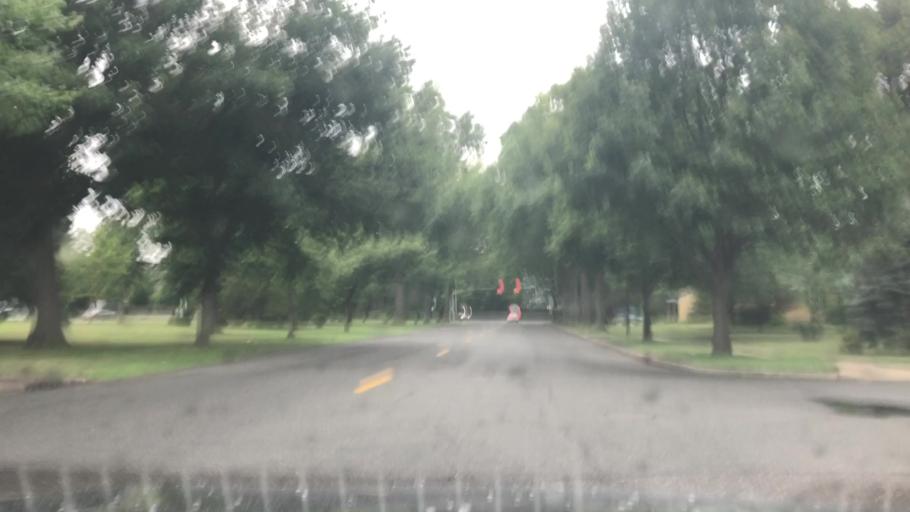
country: US
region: New York
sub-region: Nassau County
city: Garden City
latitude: 40.7142
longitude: -73.6370
